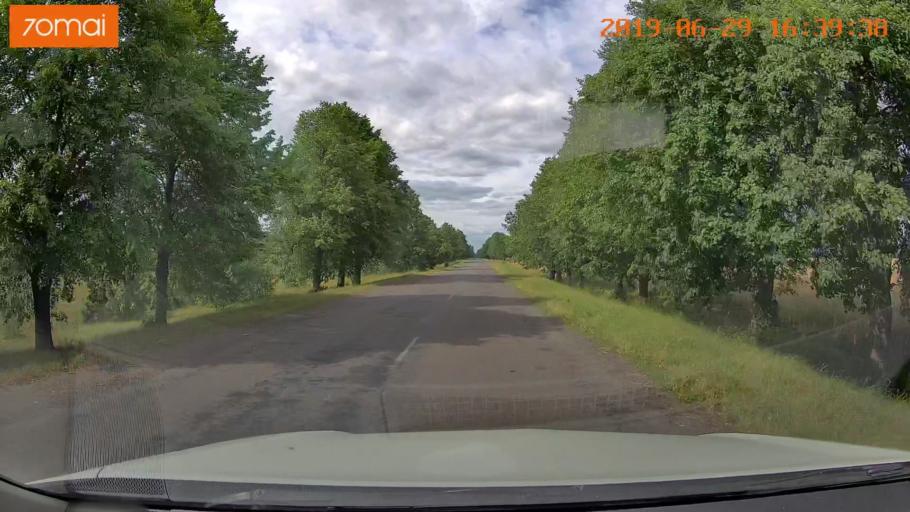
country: BY
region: Brest
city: Luninyets
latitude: 52.2449
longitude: 27.0164
